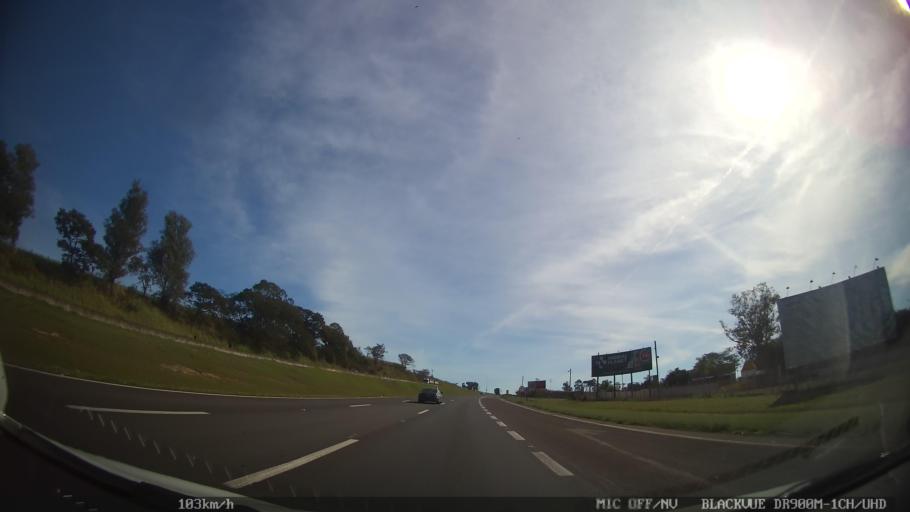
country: BR
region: Sao Paulo
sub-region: Araras
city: Araras
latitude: -22.3904
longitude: -47.3932
